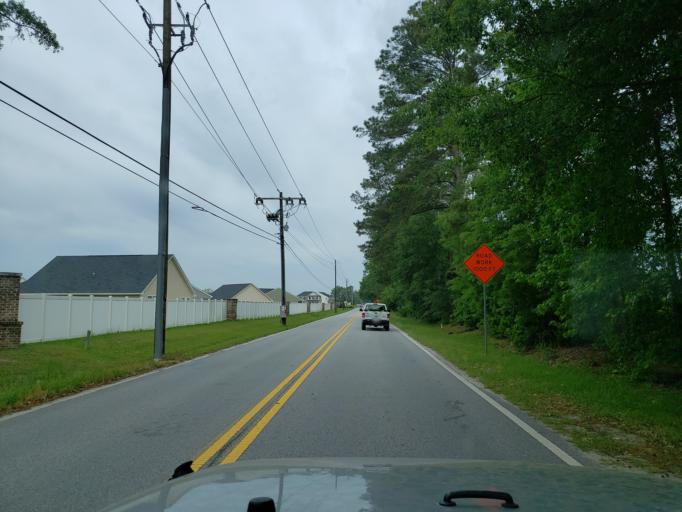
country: US
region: Georgia
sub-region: Chatham County
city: Port Wentworth
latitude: 32.1839
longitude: -81.2159
